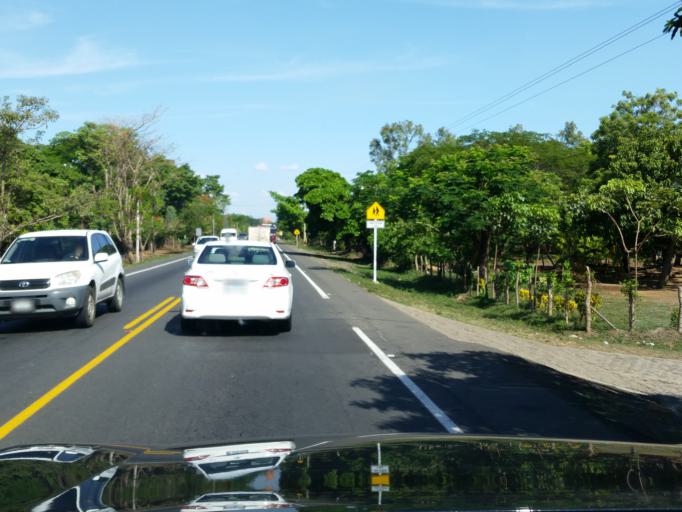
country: NI
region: Leon
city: Leon
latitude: 12.3507
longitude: -86.8279
